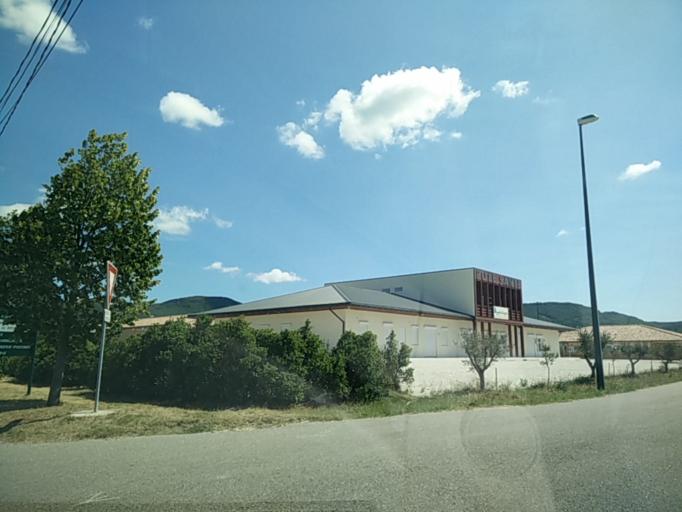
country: FR
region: Rhone-Alpes
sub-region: Departement de la Drome
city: La Begude-de-Mazenc
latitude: 44.5470
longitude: 4.9201
